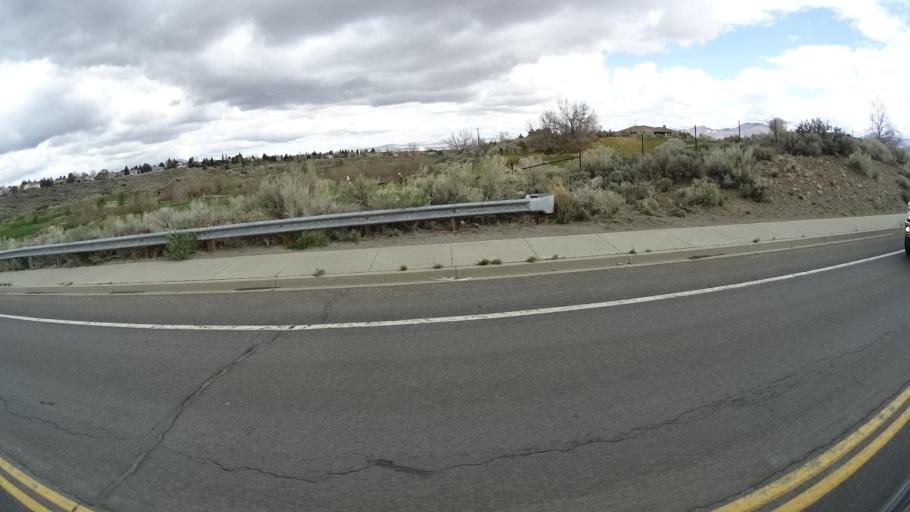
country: US
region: Nevada
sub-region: Washoe County
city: Reno
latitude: 39.4042
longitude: -119.7787
